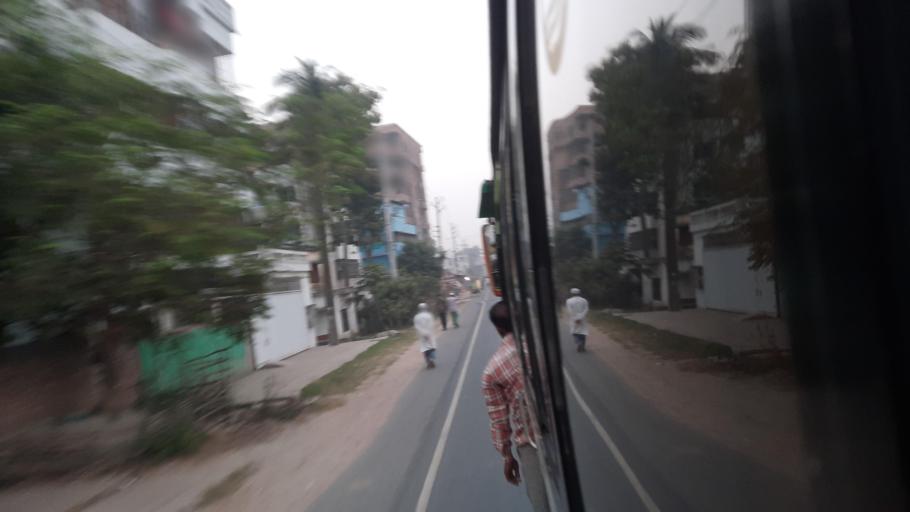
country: BD
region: Khulna
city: Jessore
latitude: 23.1760
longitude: 89.1919
